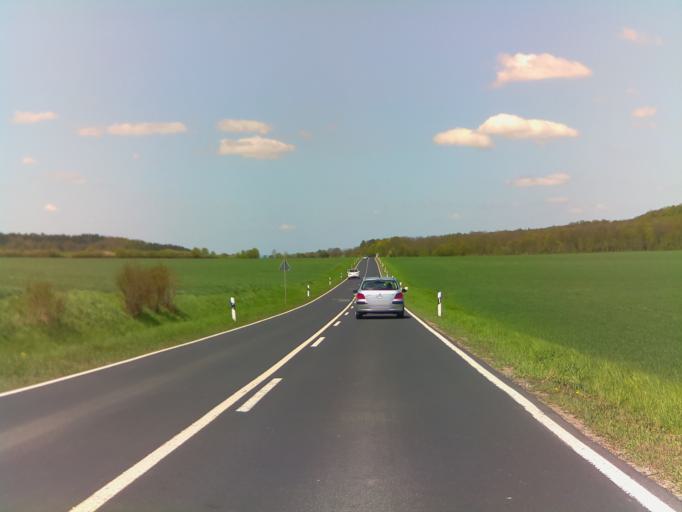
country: DE
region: Thuringia
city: Dornheim
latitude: 50.8021
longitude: 10.9814
